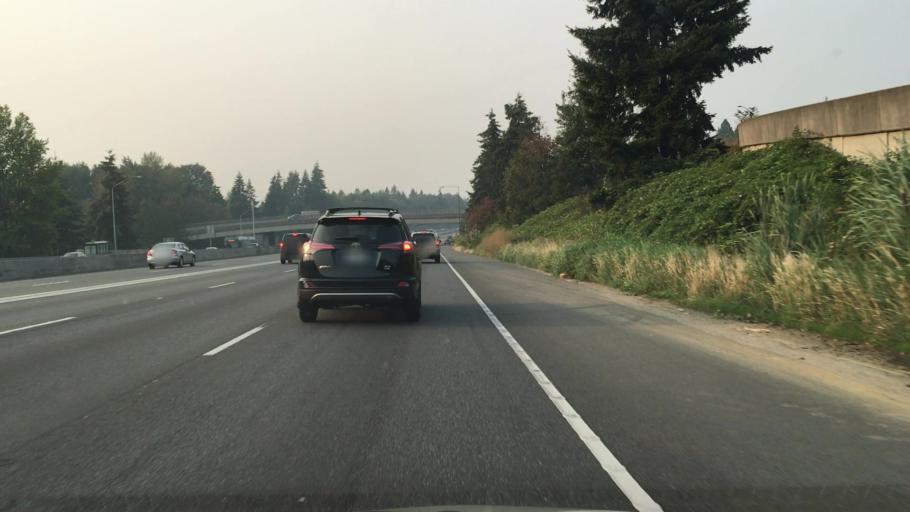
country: US
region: Washington
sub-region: King County
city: Kirkland
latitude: 47.6685
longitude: -122.1930
